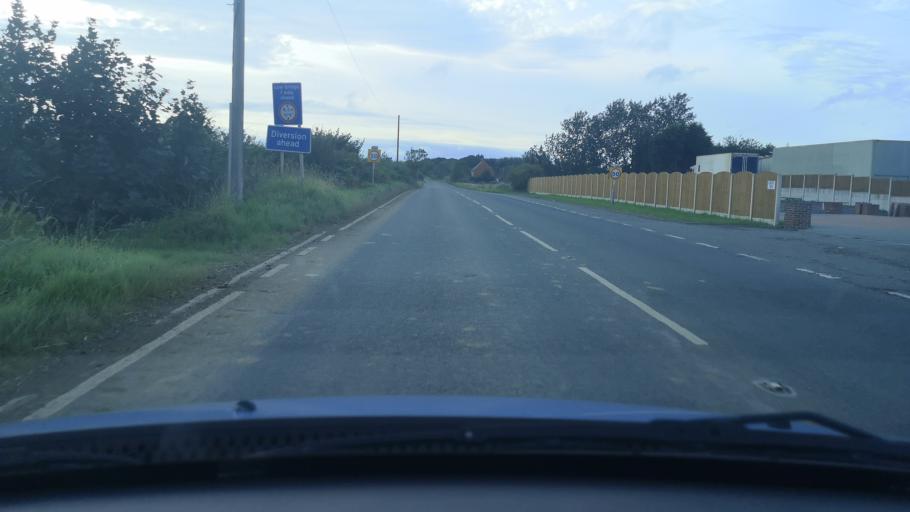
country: GB
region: England
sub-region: City and Borough of Wakefield
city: Upton
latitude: 53.6139
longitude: -1.2965
